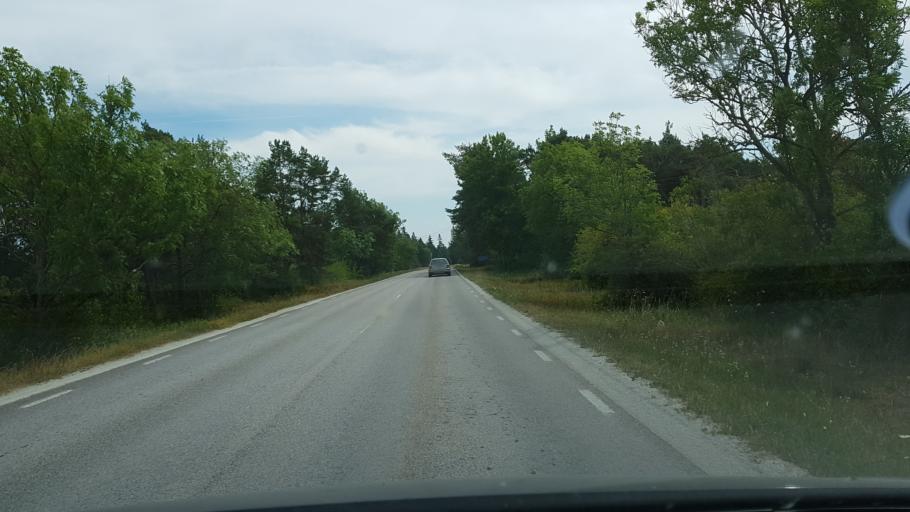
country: SE
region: Gotland
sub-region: Gotland
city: Slite
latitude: 57.7462
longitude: 18.7350
